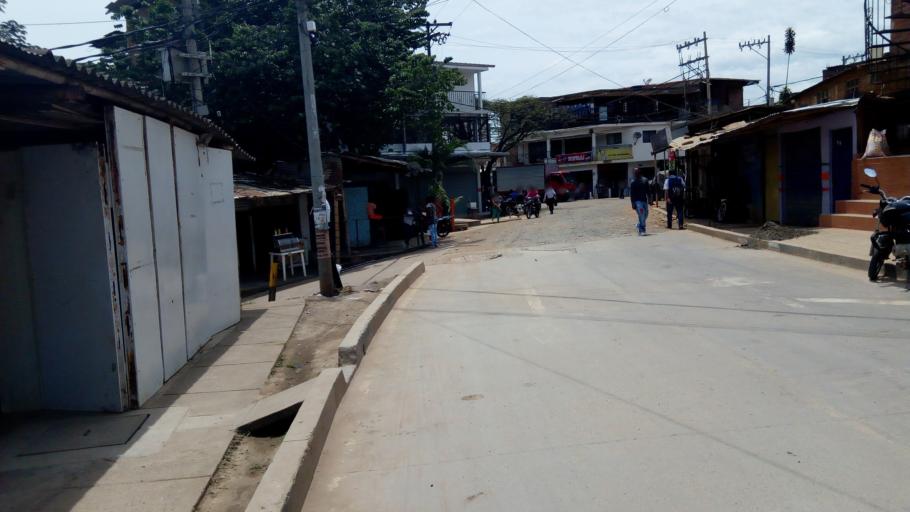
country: CO
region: Valle del Cauca
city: Cali
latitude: 3.3795
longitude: -76.5614
